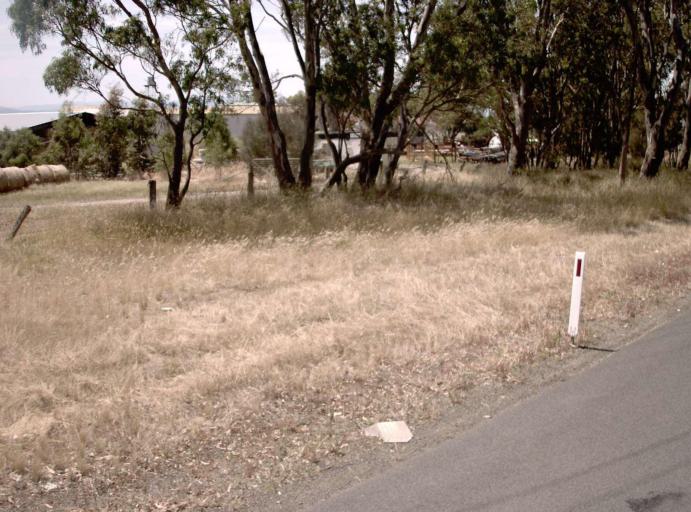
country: AU
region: Victoria
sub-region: Latrobe
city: Traralgon
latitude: -38.1674
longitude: 146.6978
